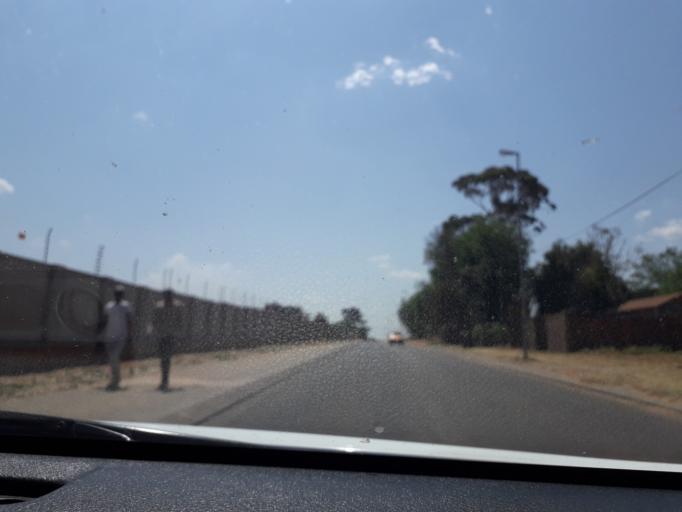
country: ZA
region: Gauteng
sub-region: City of Johannesburg Metropolitan Municipality
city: Modderfontein
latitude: -26.0791
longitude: 28.1989
